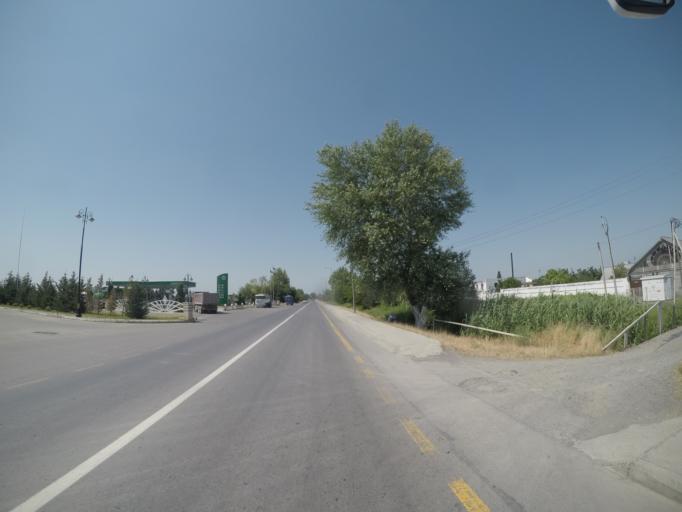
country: AZ
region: Agdas
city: Agdas
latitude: 40.6421
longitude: 47.4925
